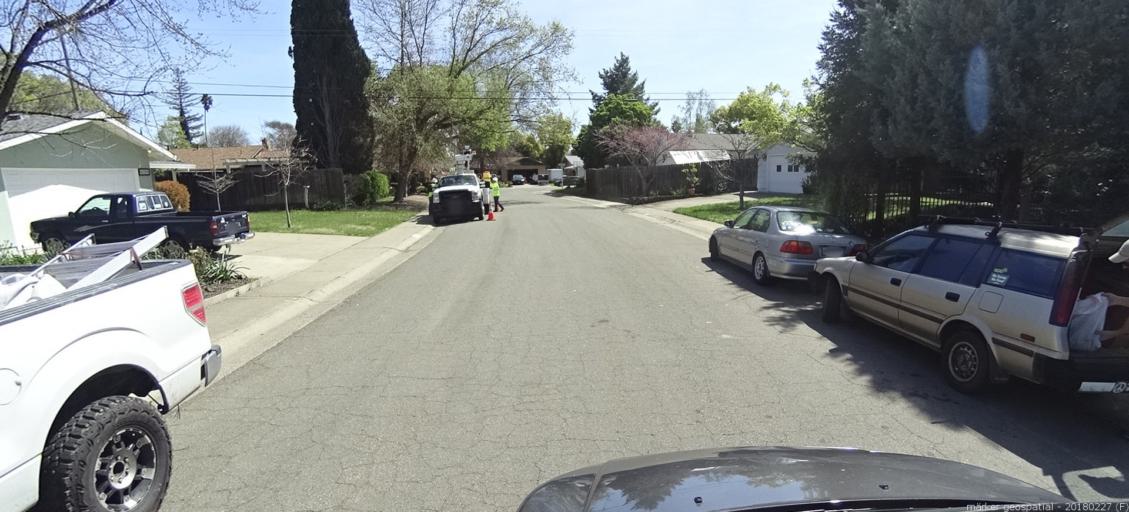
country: US
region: California
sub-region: Sacramento County
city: Rosemont
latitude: 38.5528
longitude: -121.3609
